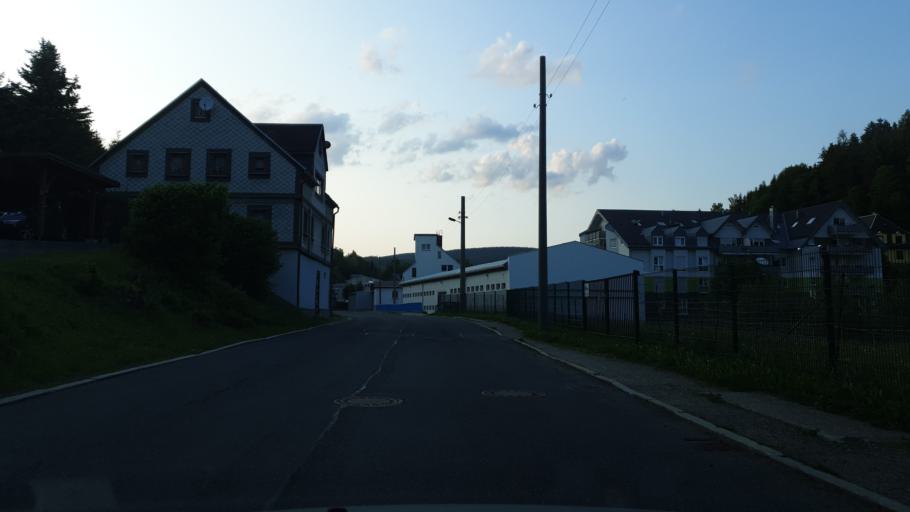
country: DE
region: Saxony
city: Klingenthal
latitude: 50.3628
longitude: 12.4681
